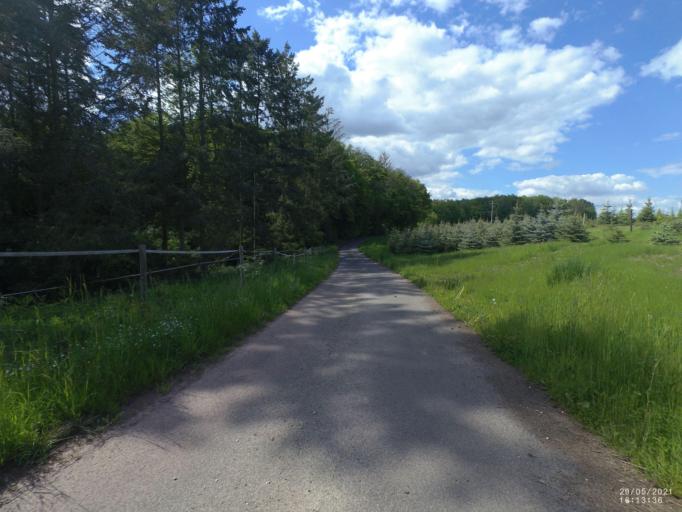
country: DE
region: Rheinland-Pfalz
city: Nortershausen
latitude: 50.2094
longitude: 7.4679
